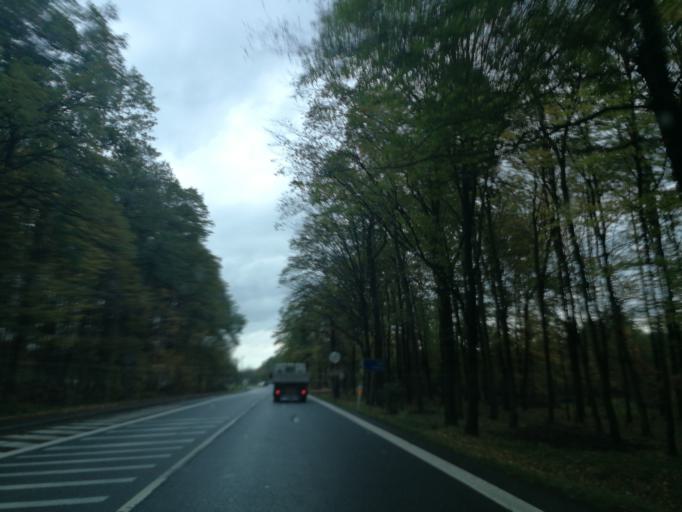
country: CZ
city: Hodslavice
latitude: 49.5226
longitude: 18.0151
